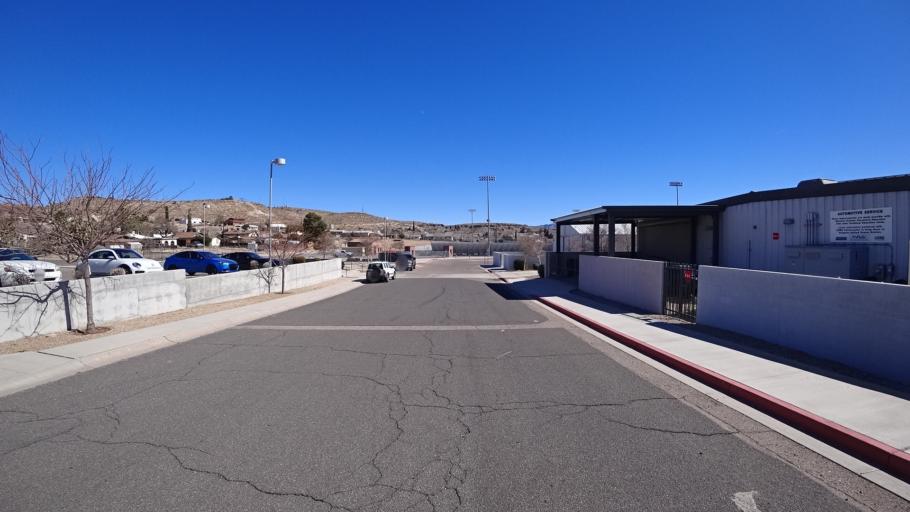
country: US
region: Arizona
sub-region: Mohave County
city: Kingman
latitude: 35.1935
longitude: -114.0606
